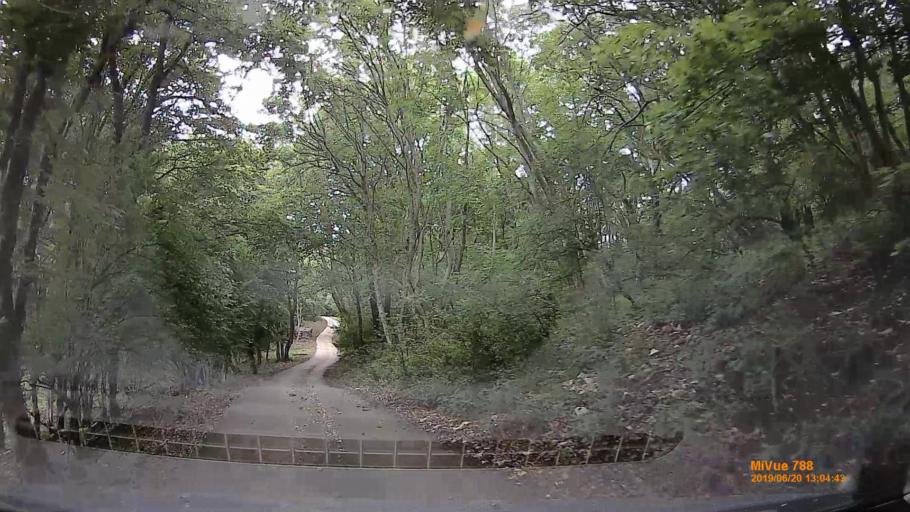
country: HU
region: Baranya
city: Hosszuheteny
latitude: 46.2143
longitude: 18.3606
